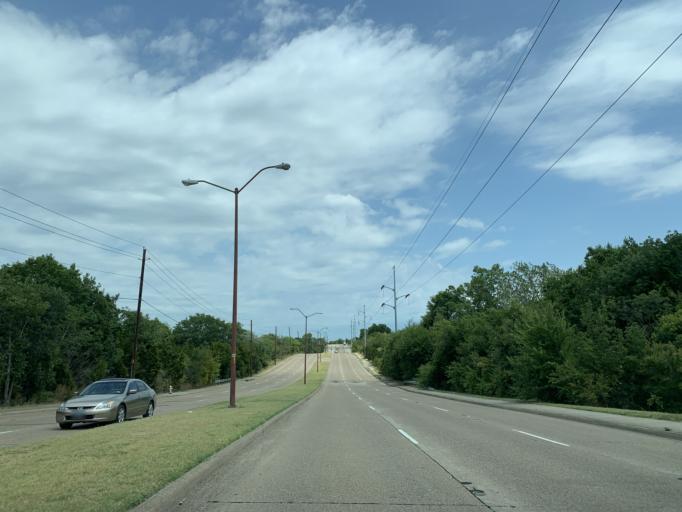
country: US
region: Texas
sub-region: Dallas County
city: DeSoto
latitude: 32.6623
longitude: -96.8111
